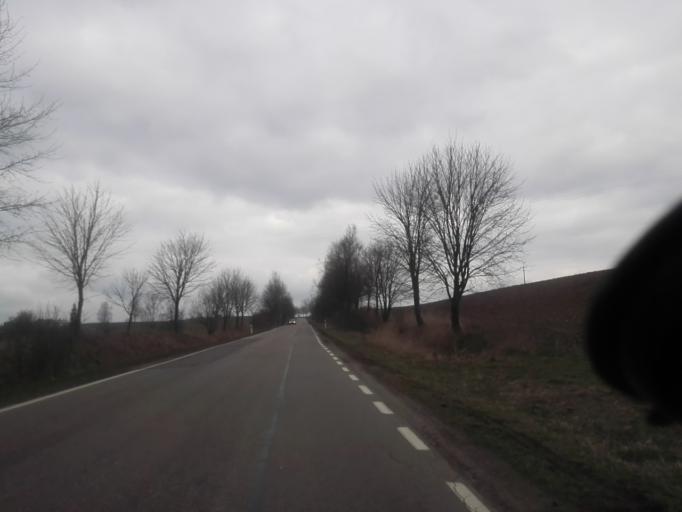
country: PL
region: Podlasie
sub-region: Suwalki
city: Suwalki
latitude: 54.2335
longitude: 22.9131
